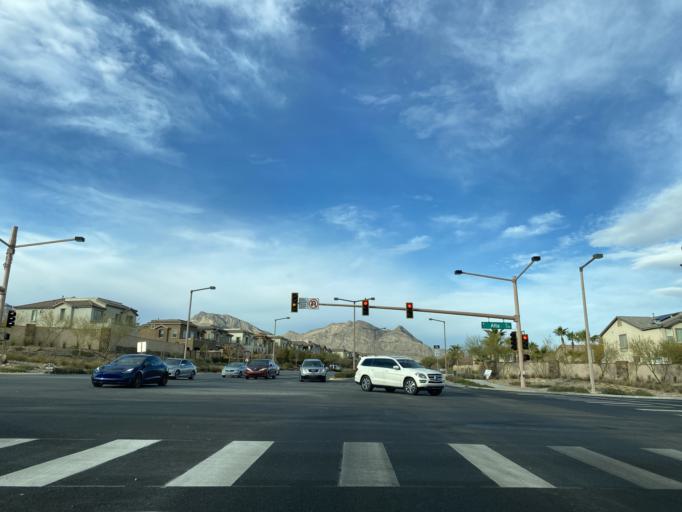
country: US
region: Nevada
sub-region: Clark County
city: Summerlin South
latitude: 36.1712
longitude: -115.3554
